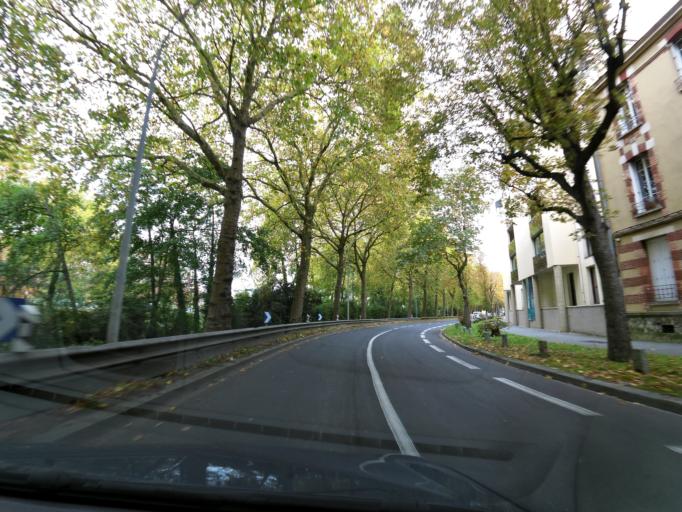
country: FR
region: Brittany
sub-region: Departement d'Ille-et-Vilaine
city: Rennes
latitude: 48.1142
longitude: -1.6876
